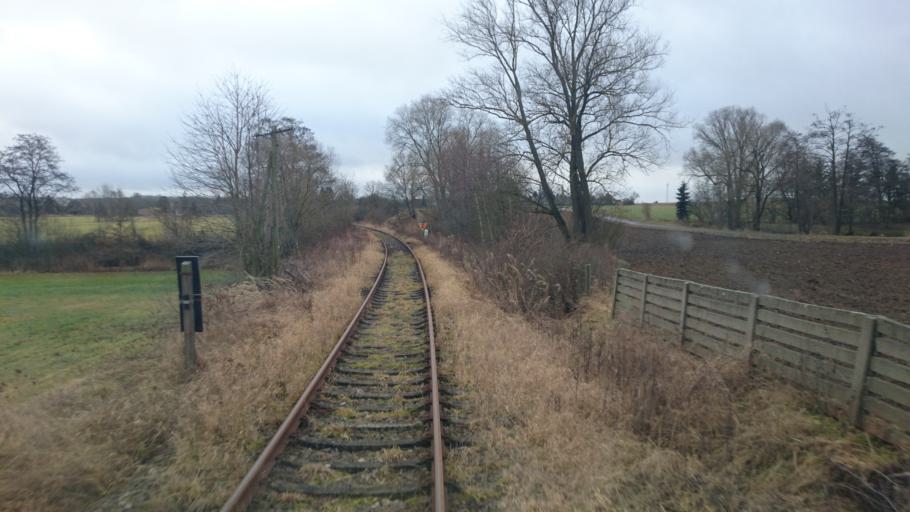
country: DE
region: Saxony
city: Muhltroff
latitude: 50.5461
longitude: 11.9191
